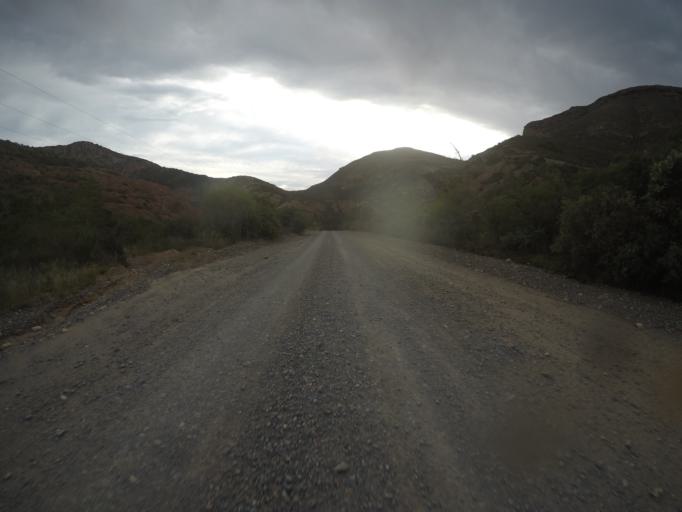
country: ZA
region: Eastern Cape
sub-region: Cacadu District Municipality
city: Willowmore
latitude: -33.5159
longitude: 23.8236
